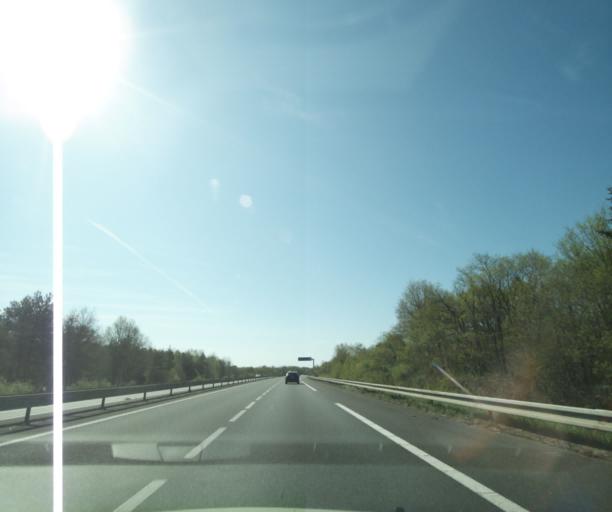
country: FR
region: Centre
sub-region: Departement du Loir-et-Cher
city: Nouan-le-Fuzelier
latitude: 47.5640
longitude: 2.0068
